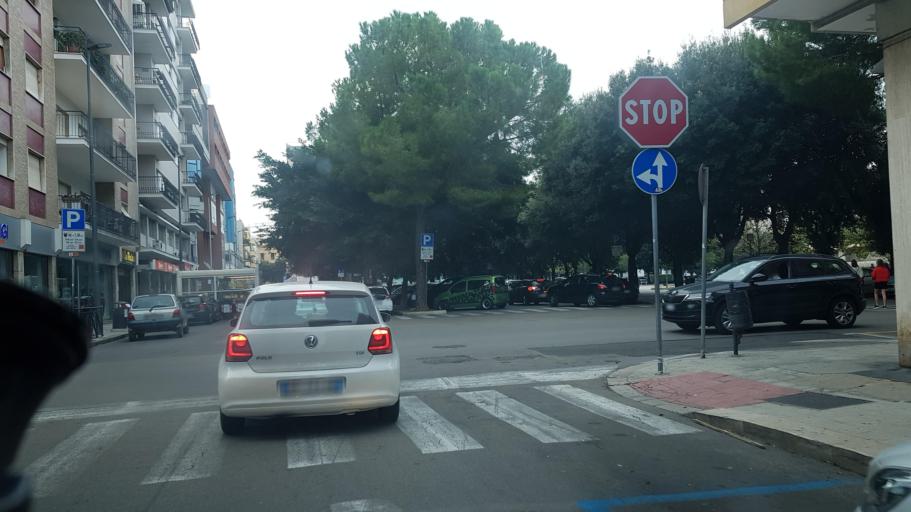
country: IT
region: Apulia
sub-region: Provincia di Lecce
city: Lecce
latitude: 40.3525
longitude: 18.1801
